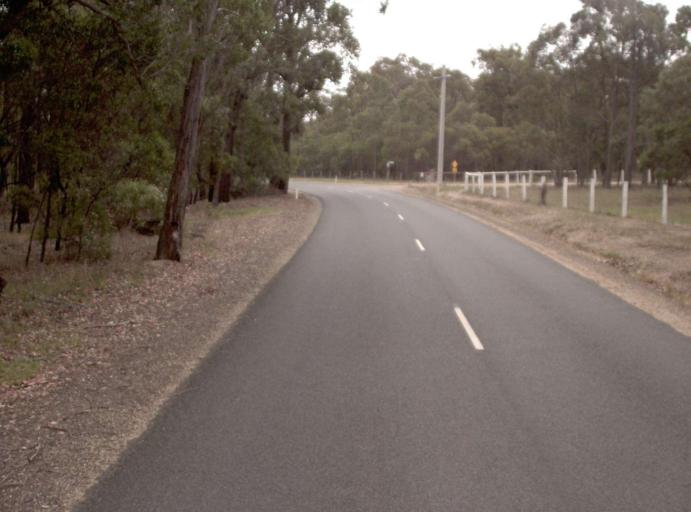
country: AU
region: Victoria
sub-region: Wellington
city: Heyfield
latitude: -37.9420
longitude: 146.7640
